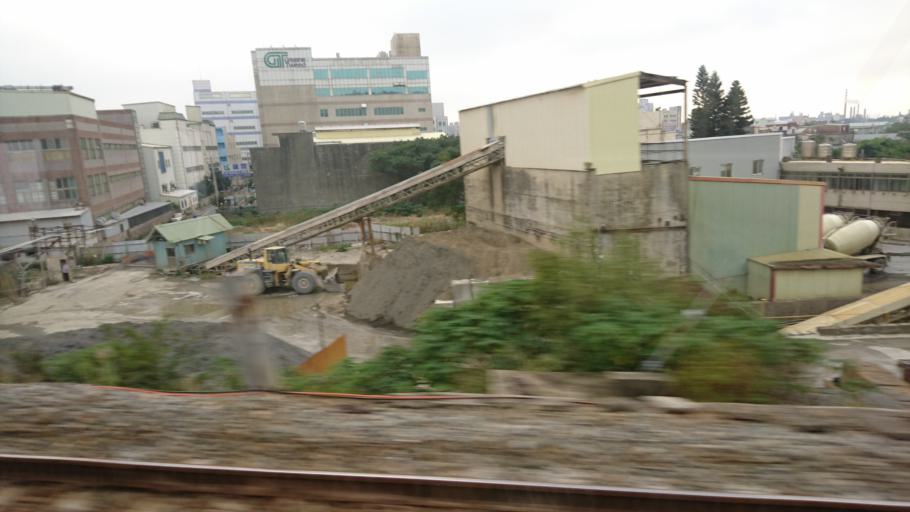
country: TW
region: Taiwan
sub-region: Hsinchu
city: Zhubei
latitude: 24.8497
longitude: 121.0137
